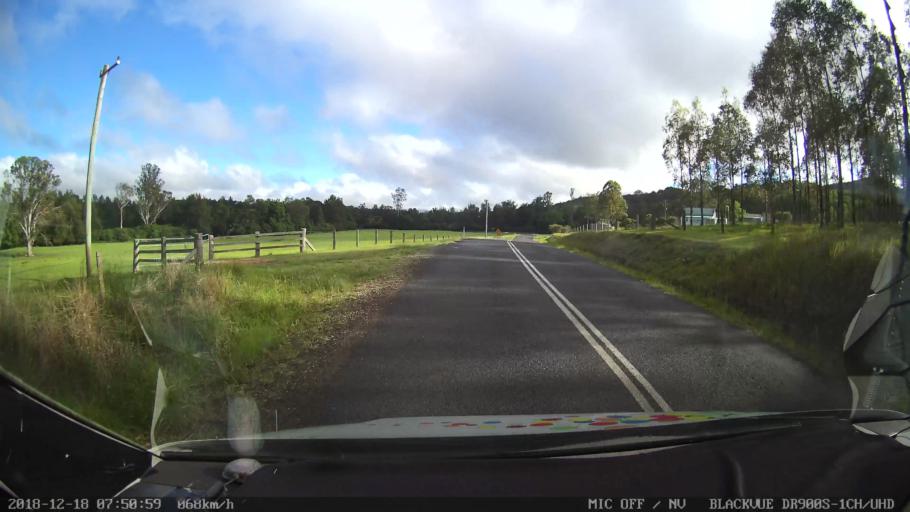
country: AU
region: New South Wales
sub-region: Kyogle
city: Kyogle
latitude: -28.4404
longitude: 152.5747
